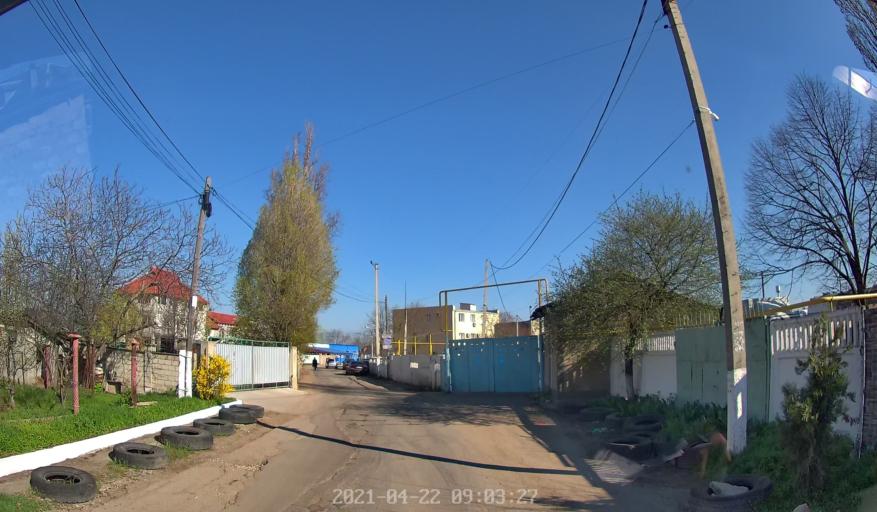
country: MD
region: Chisinau
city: Ciorescu
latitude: 47.1196
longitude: 28.8726
